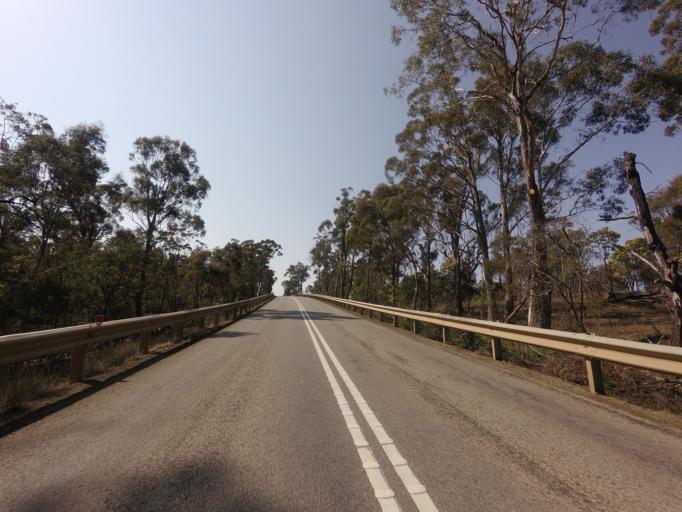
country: AU
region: Tasmania
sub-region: Northern Midlands
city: Evandale
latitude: -41.8267
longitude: 147.5057
